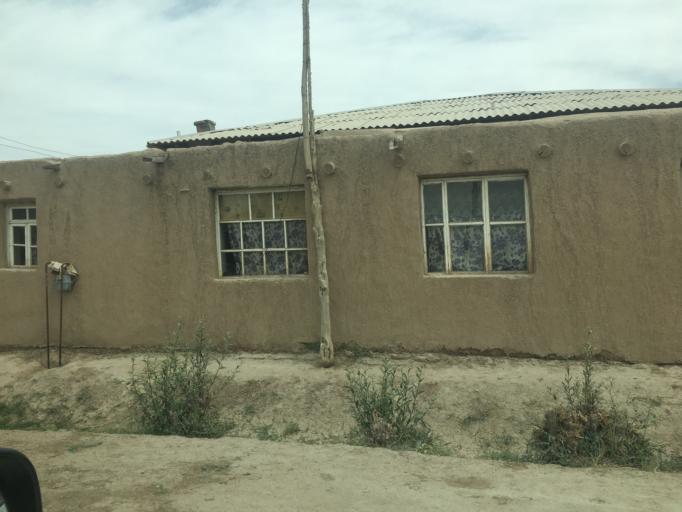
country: TM
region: Dasoguz
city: Tagta
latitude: 41.6136
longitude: 59.8545
